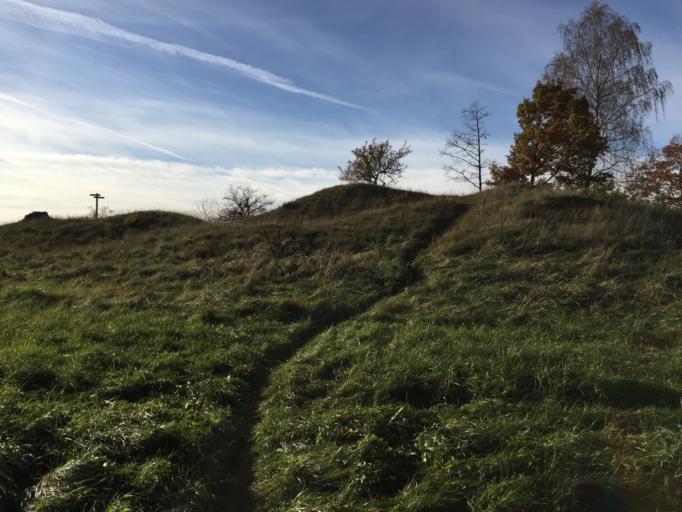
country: LV
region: Skriveri
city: Skriveri
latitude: 56.6141
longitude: 25.1545
